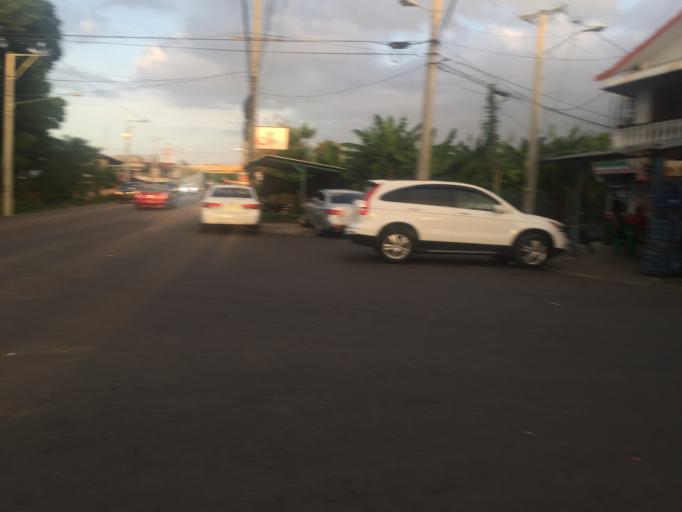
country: DO
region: Santiago
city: Licey al Medio
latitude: 19.4412
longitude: -70.6282
